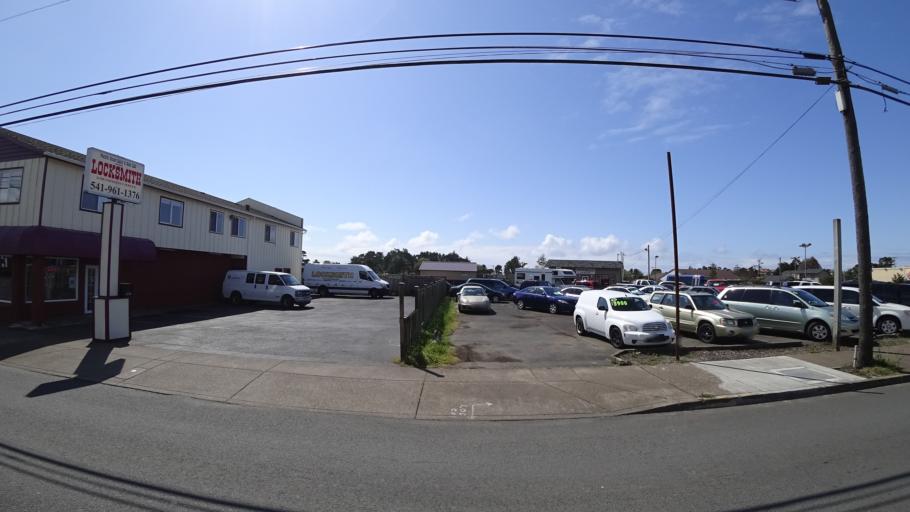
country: US
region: Oregon
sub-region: Lincoln County
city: Newport
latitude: 44.6471
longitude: -124.0531
